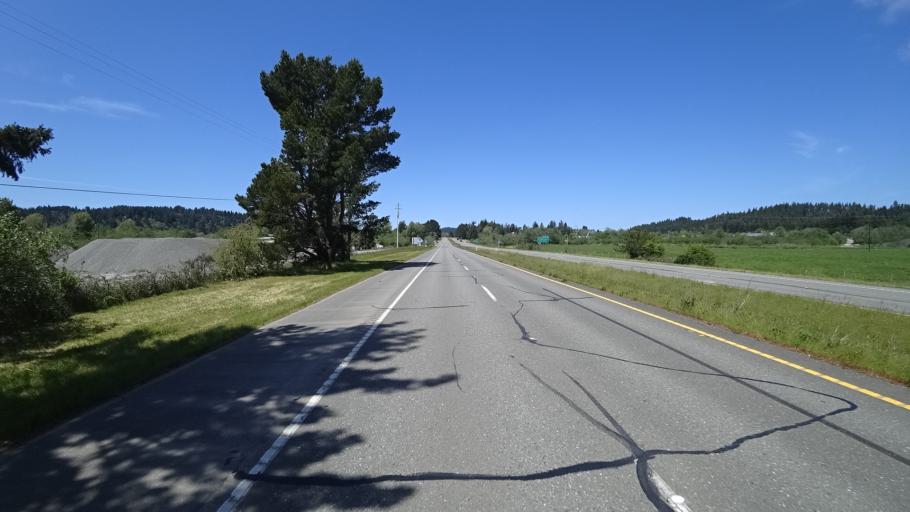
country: US
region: California
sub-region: Humboldt County
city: Blue Lake
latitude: 40.8950
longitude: -124.0150
